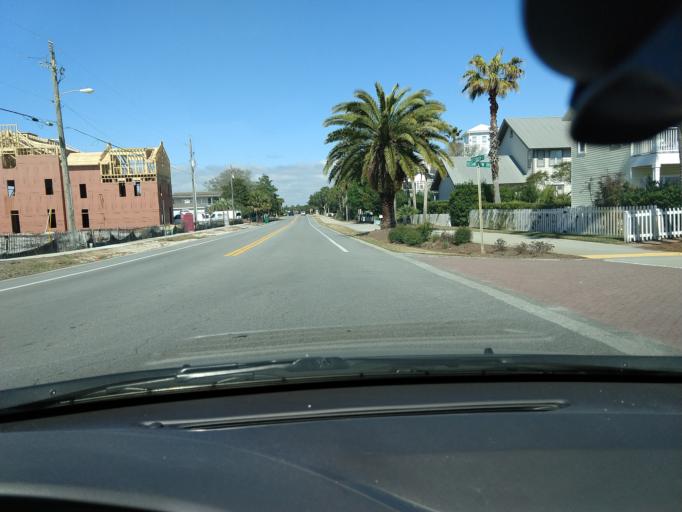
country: US
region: Florida
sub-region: Walton County
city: Miramar Beach
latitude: 30.3835
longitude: -86.4260
